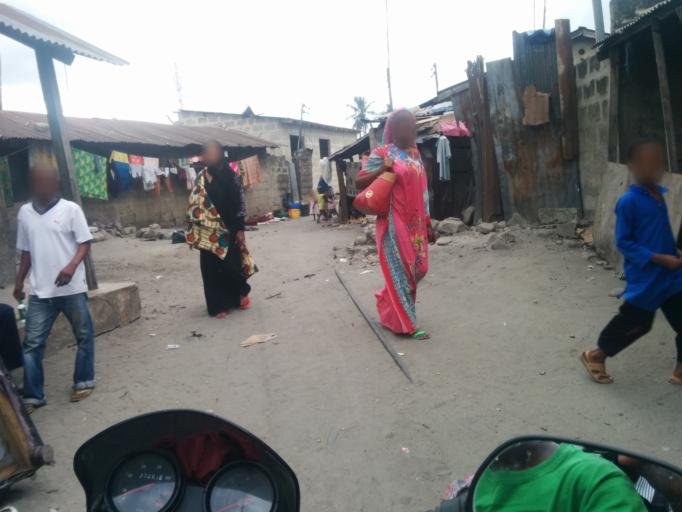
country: TZ
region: Dar es Salaam
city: Dar es Salaam
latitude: -6.8346
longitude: 39.2783
